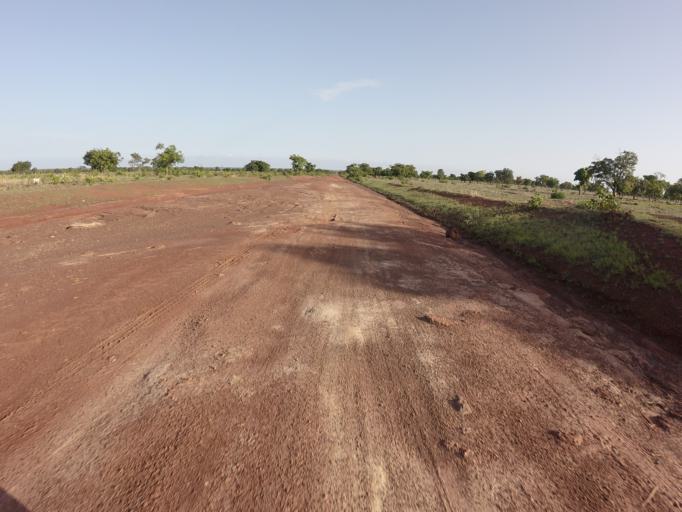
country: TG
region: Savanes
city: Sansanne-Mango
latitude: 10.3817
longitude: -0.0948
